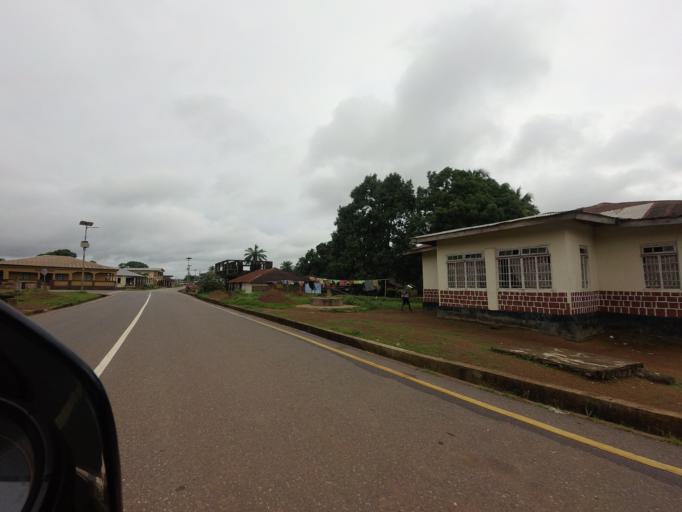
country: SL
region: Northern Province
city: Kambia
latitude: 9.1292
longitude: -12.9198
